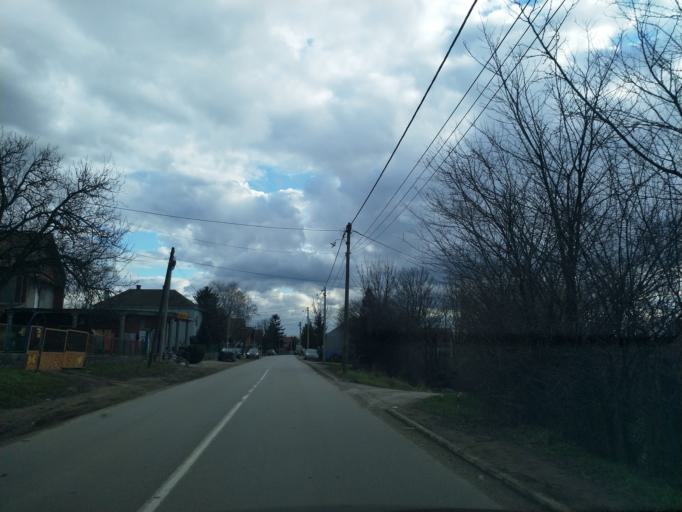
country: RS
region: Central Serbia
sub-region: Belgrade
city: Grocka
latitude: 44.6087
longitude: 20.7244
